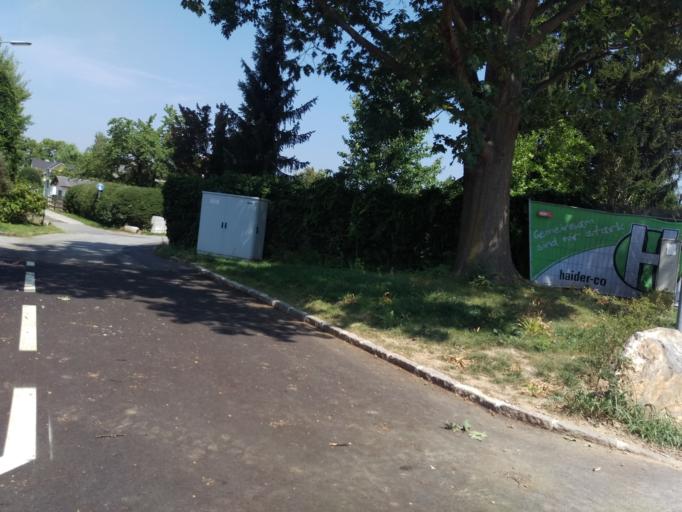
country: AT
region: Styria
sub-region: Graz Stadt
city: Graz
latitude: 47.0484
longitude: 15.4709
